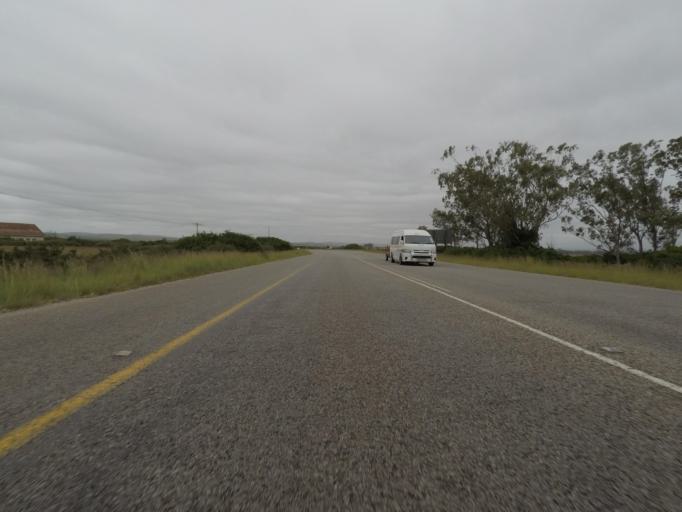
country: ZA
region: Eastern Cape
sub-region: Nelson Mandela Bay Metropolitan Municipality
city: Port Elizabeth
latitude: -33.6737
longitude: 25.8530
